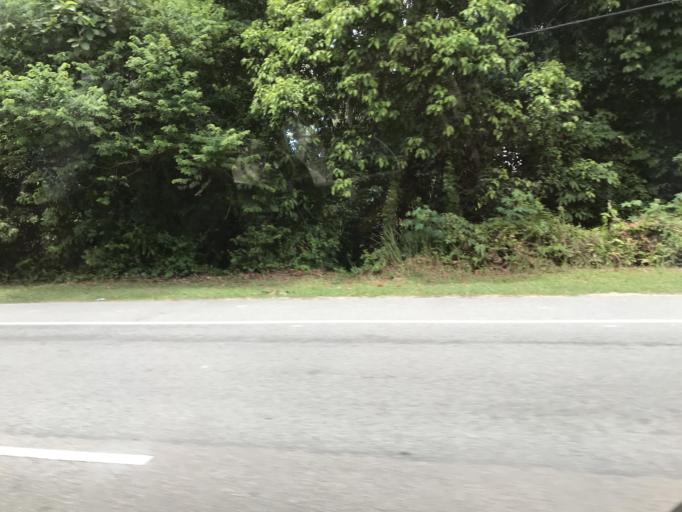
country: MY
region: Kelantan
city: Tumpat
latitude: 6.1721
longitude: 102.2098
